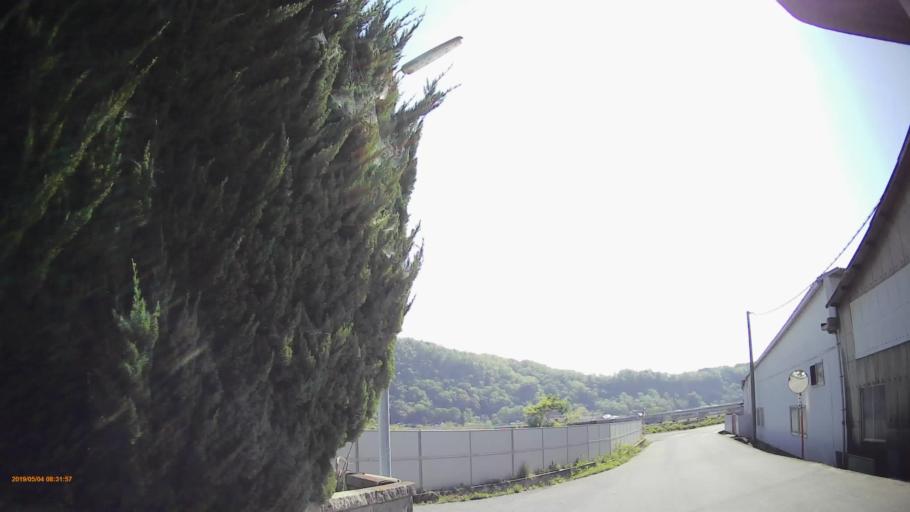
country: JP
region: Yamanashi
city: Nirasaki
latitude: 35.7314
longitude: 138.4166
